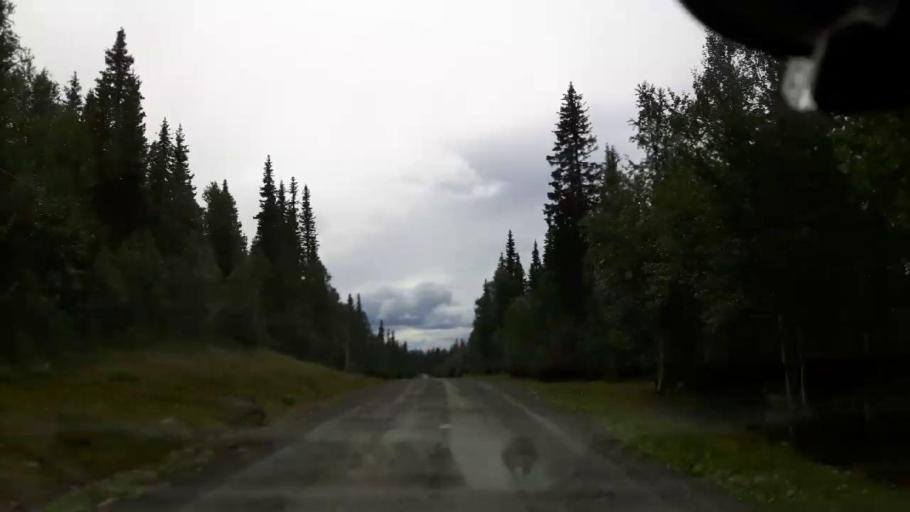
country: SE
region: Jaemtland
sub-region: Krokoms Kommun
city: Valla
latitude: 63.7524
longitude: 13.8355
